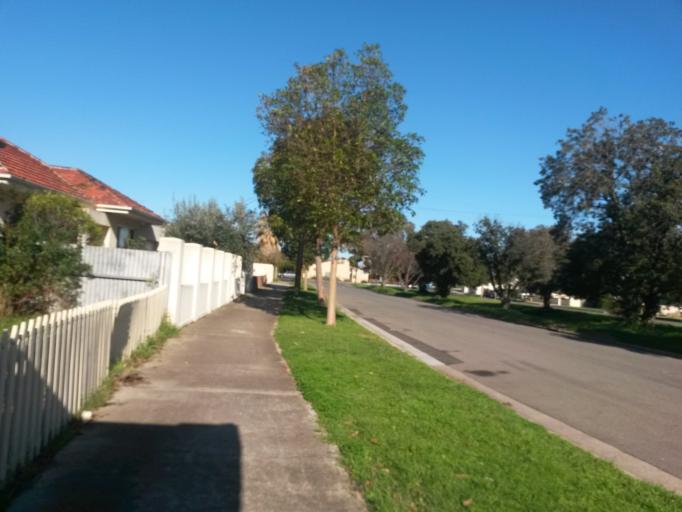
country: AU
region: South Australia
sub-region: Port Adelaide Enfield
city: Alberton
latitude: -34.8499
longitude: 138.5254
